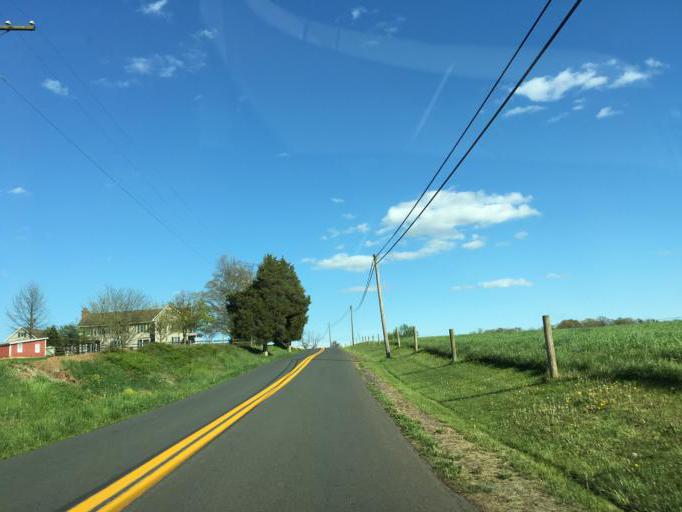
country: US
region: Maryland
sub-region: Frederick County
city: Woodsboro
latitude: 39.6214
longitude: -77.2817
